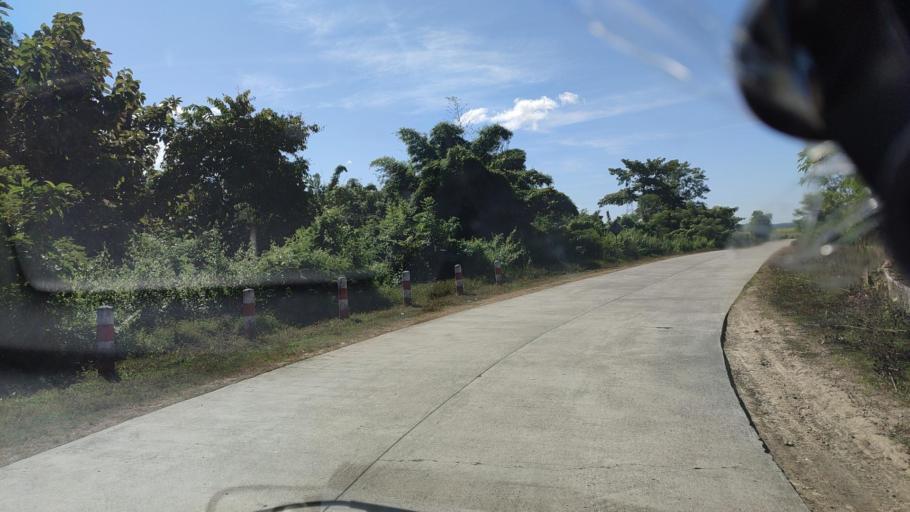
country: MM
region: Rakhine
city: Sittwe
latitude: 20.3286
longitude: 93.3420
